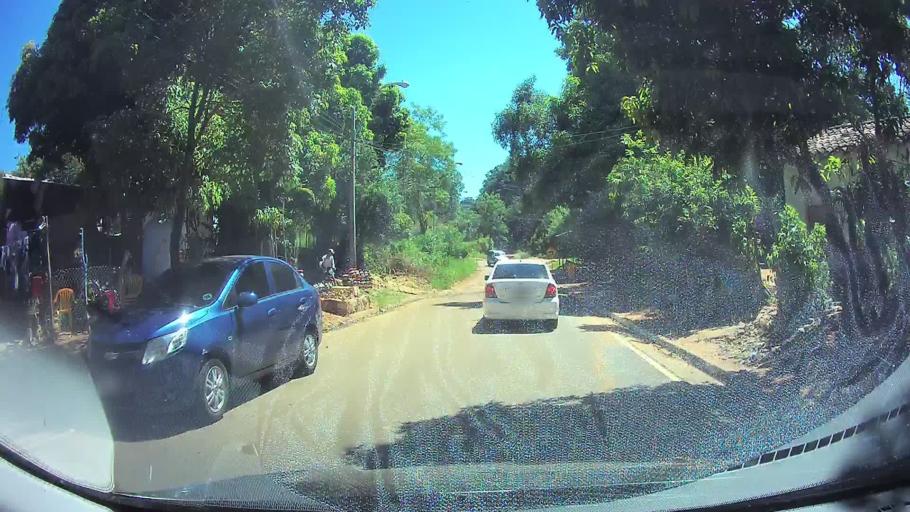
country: PY
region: Central
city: Aregua
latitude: -25.3169
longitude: -57.3902
